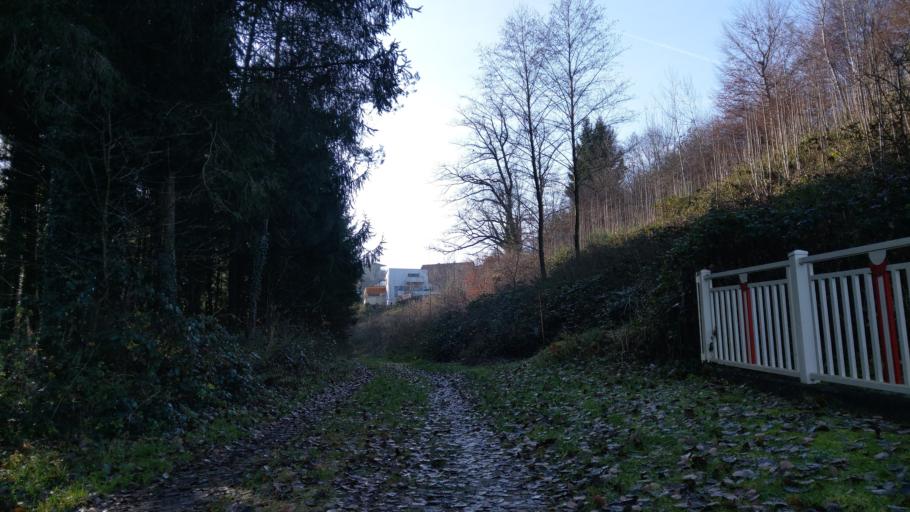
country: AT
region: Styria
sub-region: Politischer Bezirk Graz-Umgebung
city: Hart bei Graz
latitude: 47.0701
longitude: 15.5068
